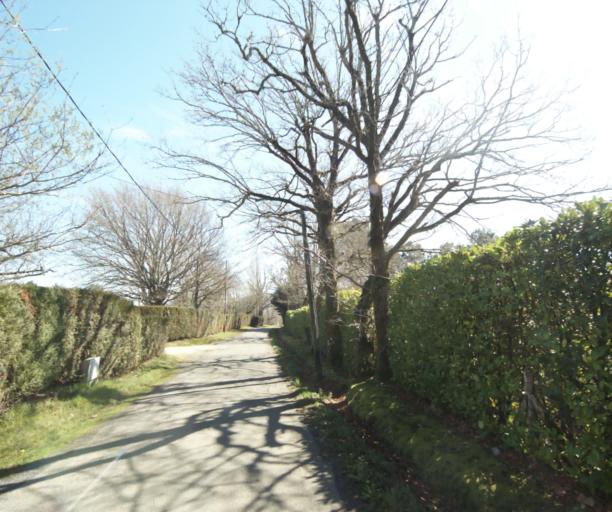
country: FR
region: Aquitaine
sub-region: Departement des Pyrenees-Atlantiques
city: Ascain
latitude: 43.3529
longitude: -1.6541
